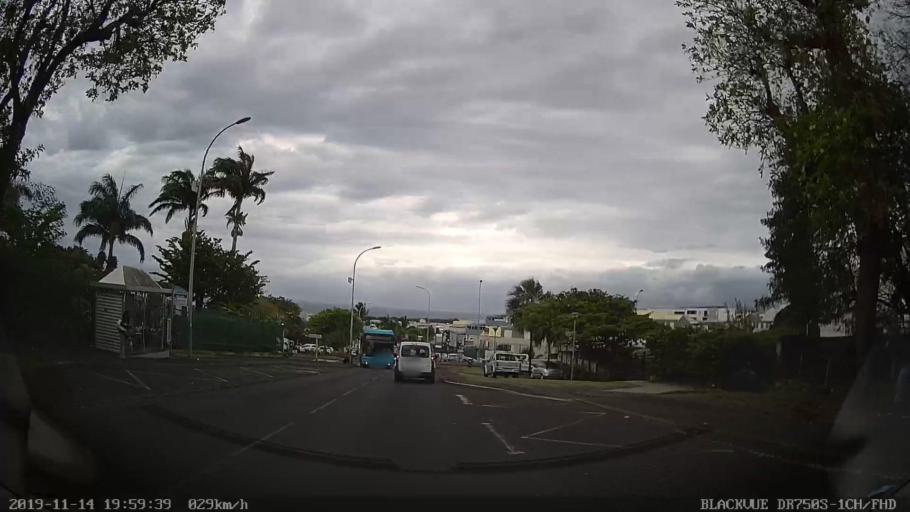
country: RE
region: Reunion
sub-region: Reunion
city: Saint-Denis
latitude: -20.9035
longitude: 55.4879
